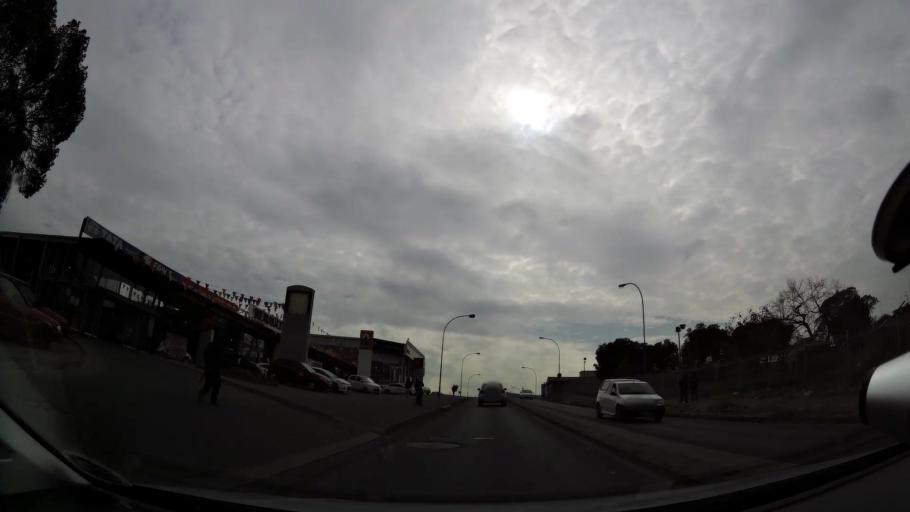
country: ZA
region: Orange Free State
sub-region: Mangaung Metropolitan Municipality
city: Bloemfontein
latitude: -29.1249
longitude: 26.2199
